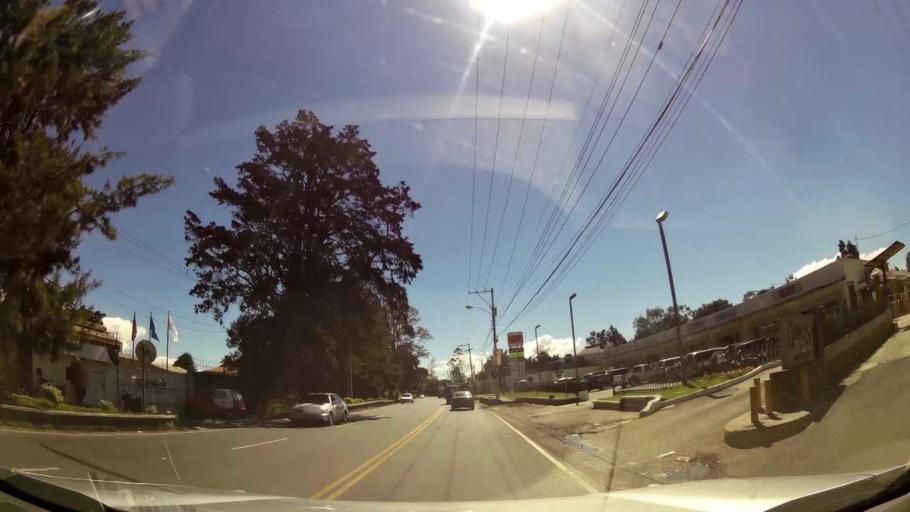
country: GT
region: Guatemala
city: San Jose Pinula
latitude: 14.5347
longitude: -90.4498
